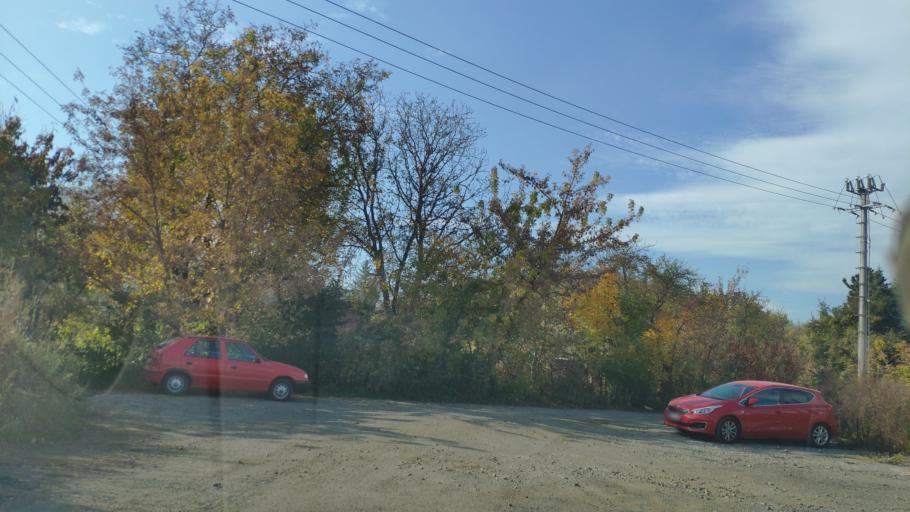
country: SK
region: Kosicky
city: Kosice
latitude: 48.6909
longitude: 21.2585
